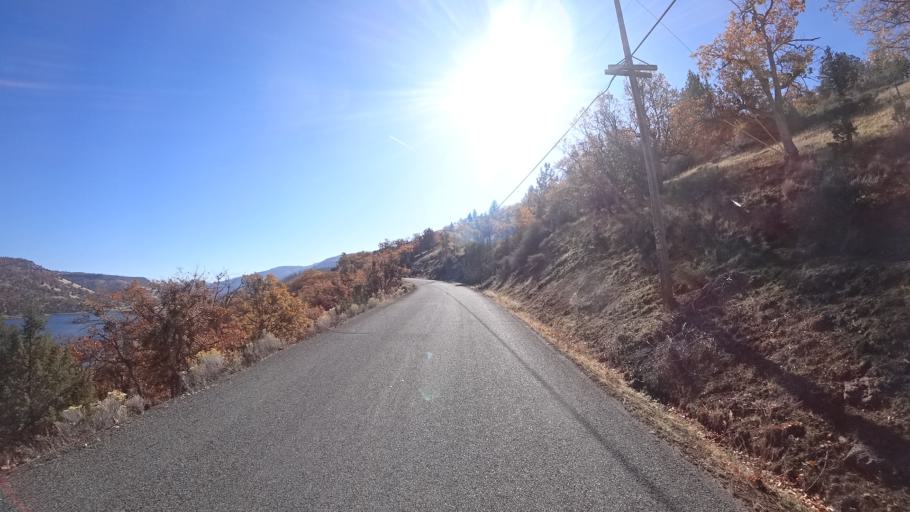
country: US
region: California
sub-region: Siskiyou County
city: Montague
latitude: 41.9787
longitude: -122.3056
